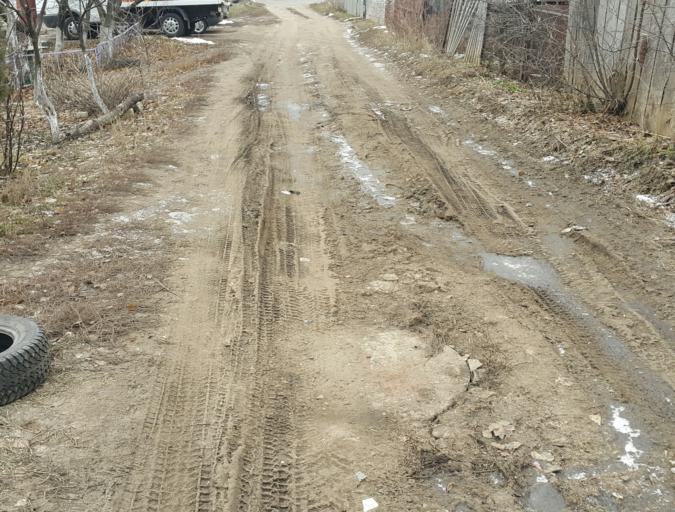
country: RU
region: Tambov
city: Pokrovo-Prigorodnoye
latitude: 52.7225
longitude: 41.4021
